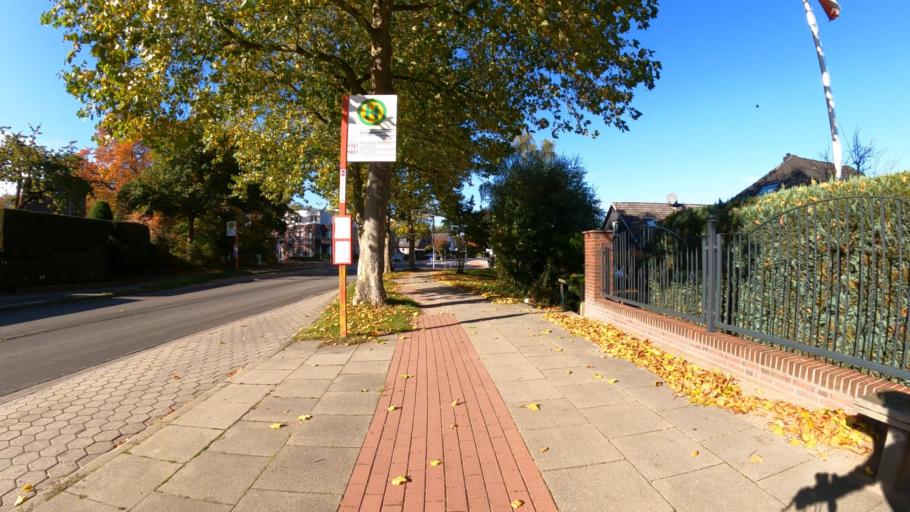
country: DE
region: Schleswig-Holstein
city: Ahrensburg
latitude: 53.6835
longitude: 10.2324
